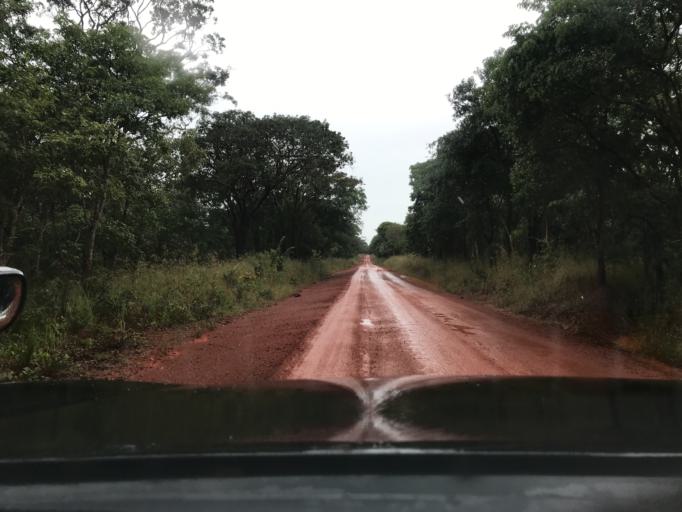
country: TZ
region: Kigoma
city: Uvinza
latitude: -5.2863
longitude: 30.3691
